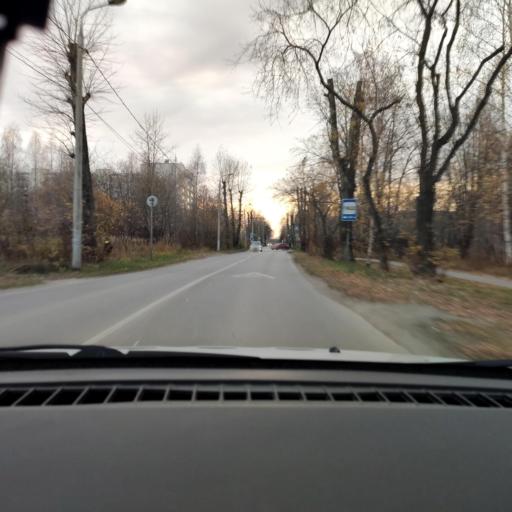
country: RU
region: Perm
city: Polazna
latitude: 58.1201
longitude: 56.3862
